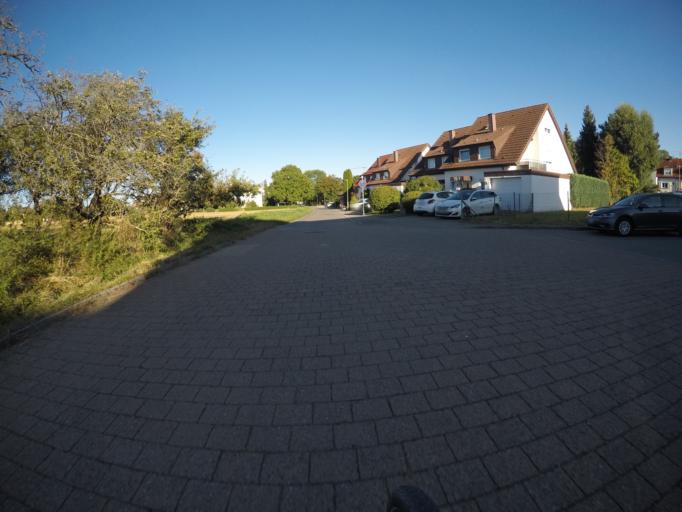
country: DE
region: Baden-Wuerttemberg
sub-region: Regierungsbezirk Stuttgart
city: Weil im Schonbuch
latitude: 48.6222
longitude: 9.0495
